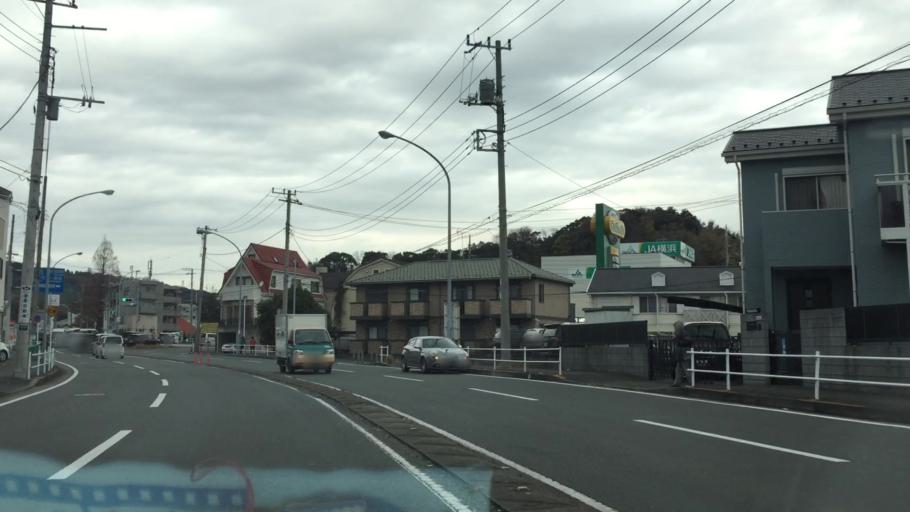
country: JP
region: Kanagawa
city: Zushi
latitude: 35.3438
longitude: 139.6118
